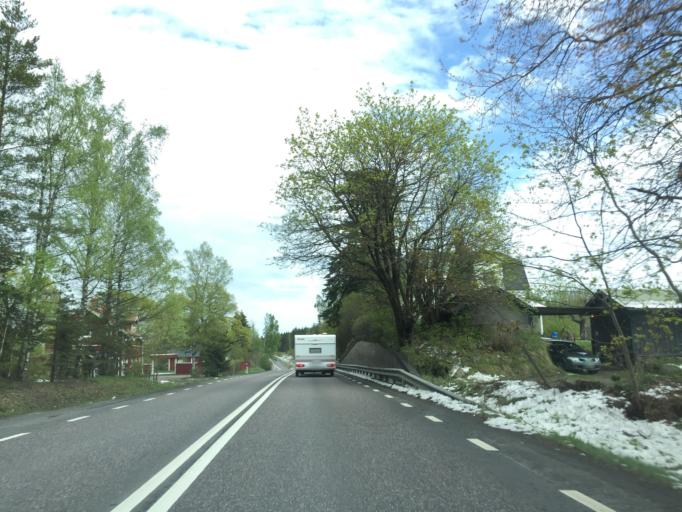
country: SE
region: Dalarna
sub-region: Ludvika Kommun
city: Ludvika
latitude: 60.1044
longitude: 15.1018
